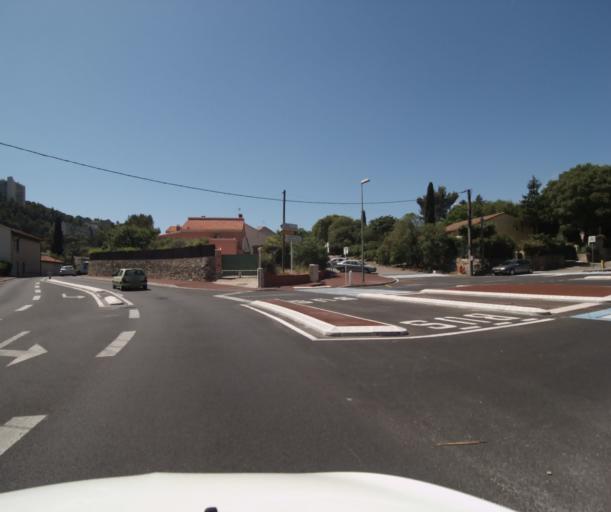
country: FR
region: Provence-Alpes-Cote d'Azur
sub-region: Departement du Var
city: Le Revest-les-Eaux
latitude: 43.1533
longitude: 5.9151
